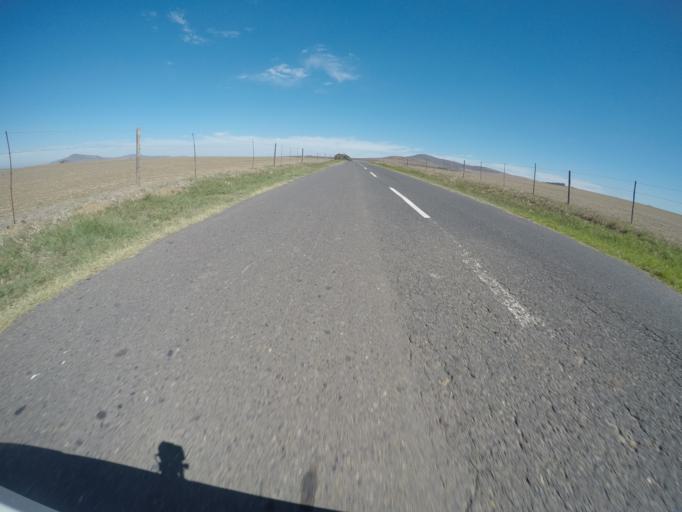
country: ZA
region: Western Cape
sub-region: City of Cape Town
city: Atlantis
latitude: -33.6891
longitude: 18.5960
